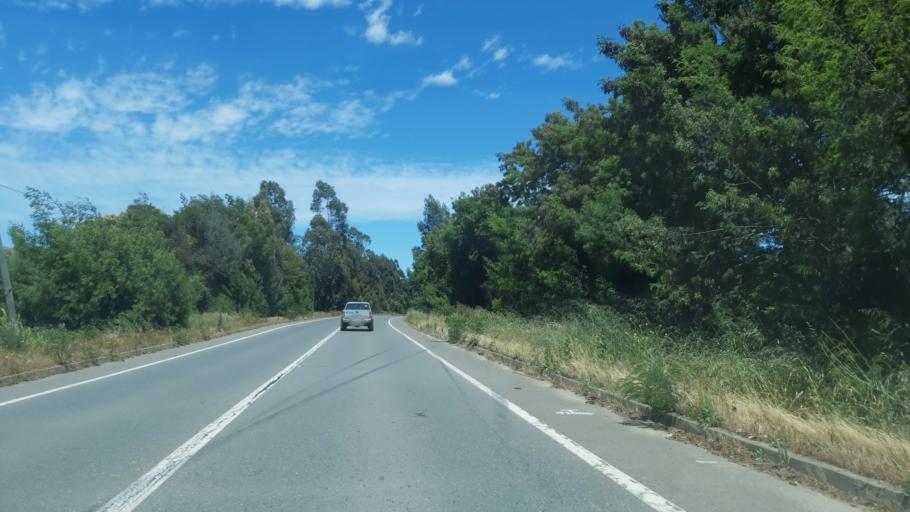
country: CL
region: Maule
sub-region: Provincia de Talca
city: Constitucion
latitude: -35.3017
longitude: -72.3750
